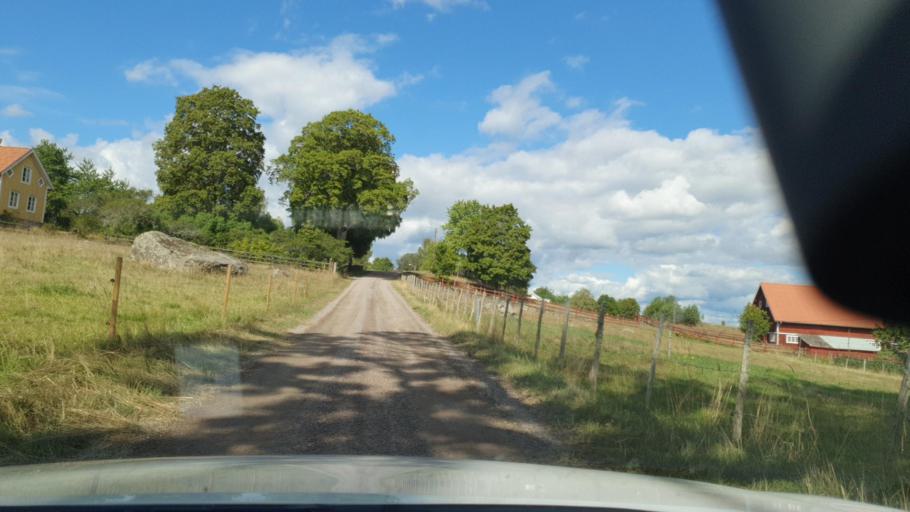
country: SE
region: Kalmar
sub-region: Hultsfreds Kommun
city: Malilla
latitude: 57.3122
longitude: 15.8197
